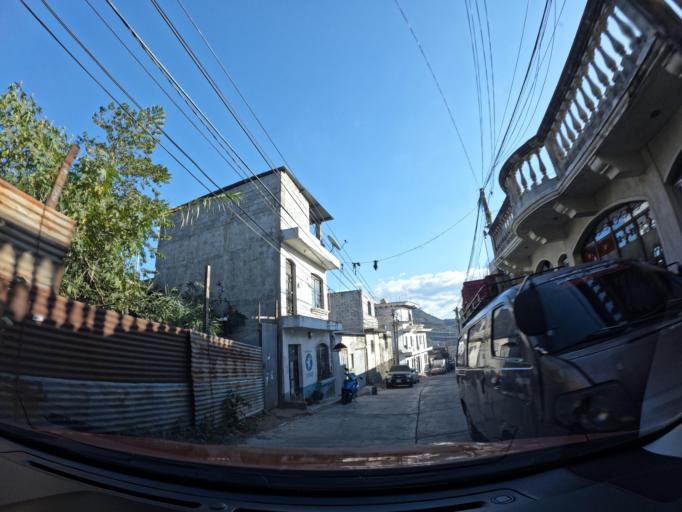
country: GT
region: Escuintla
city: Palin
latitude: 14.4071
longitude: -90.6985
